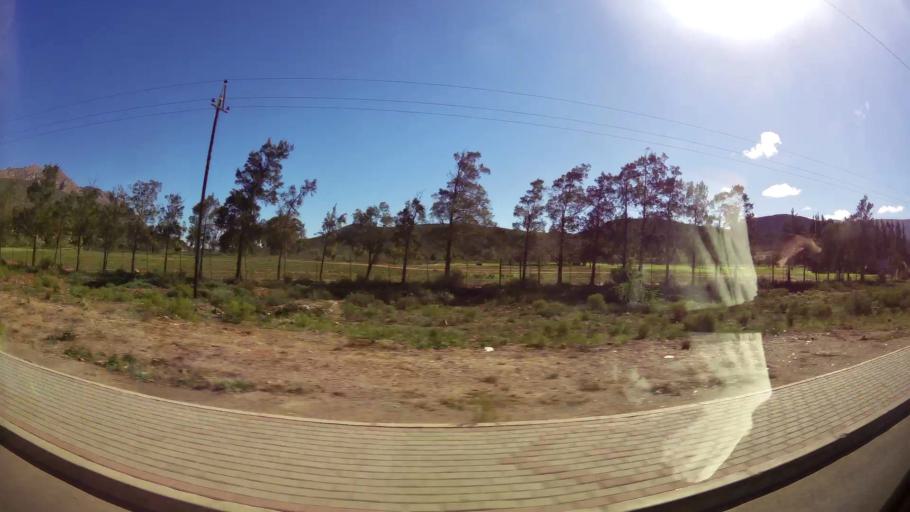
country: ZA
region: Western Cape
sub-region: Cape Winelands District Municipality
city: Ashton
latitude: -33.7722
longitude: 20.1375
